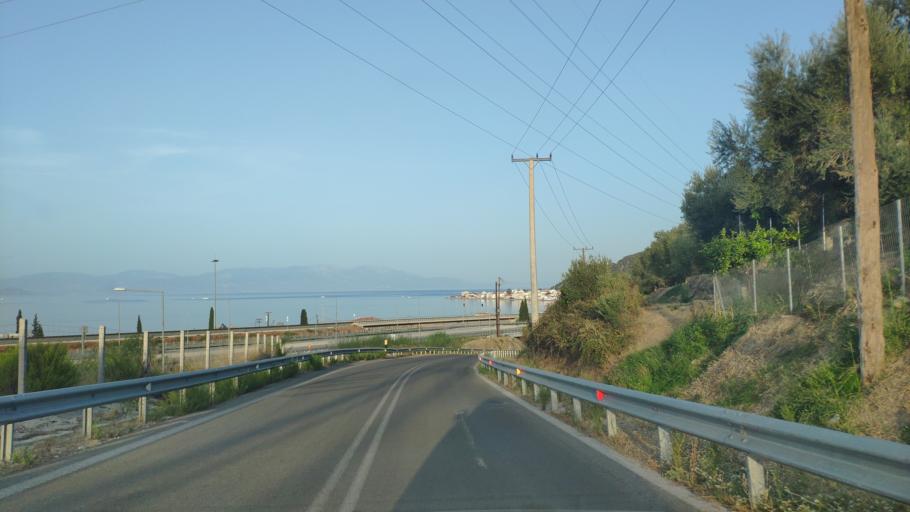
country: GR
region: West Greece
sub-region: Nomos Achaias
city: Aiyira
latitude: 38.1303
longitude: 22.4032
